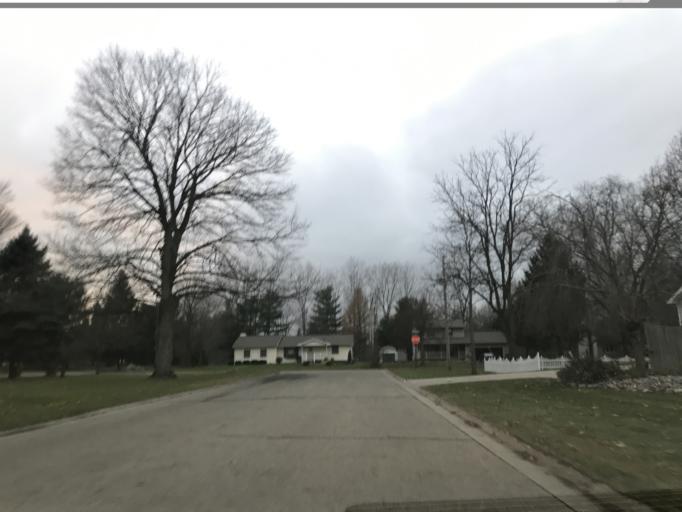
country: US
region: Michigan
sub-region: Eaton County
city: Dimondale
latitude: 42.6569
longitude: -84.6414
